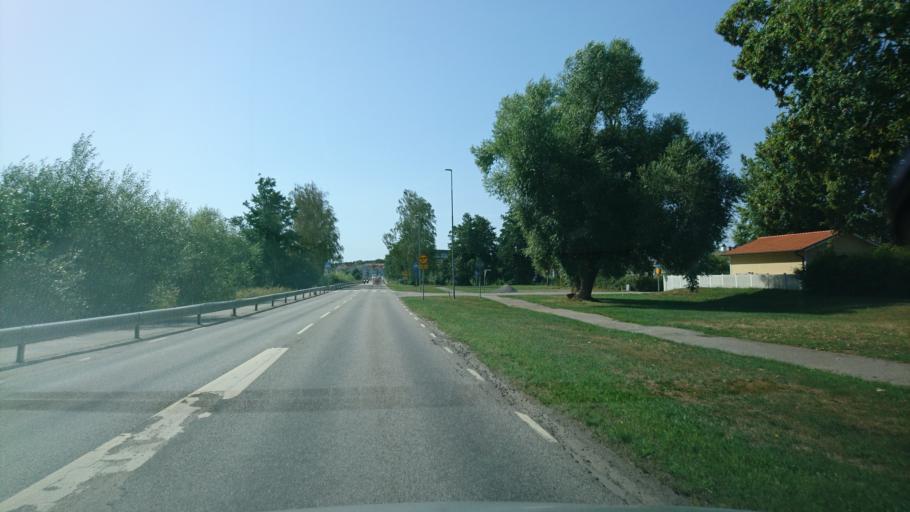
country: SE
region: Soedermanland
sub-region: Strangnas Kommun
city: Strangnas
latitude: 59.3823
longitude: 17.0402
